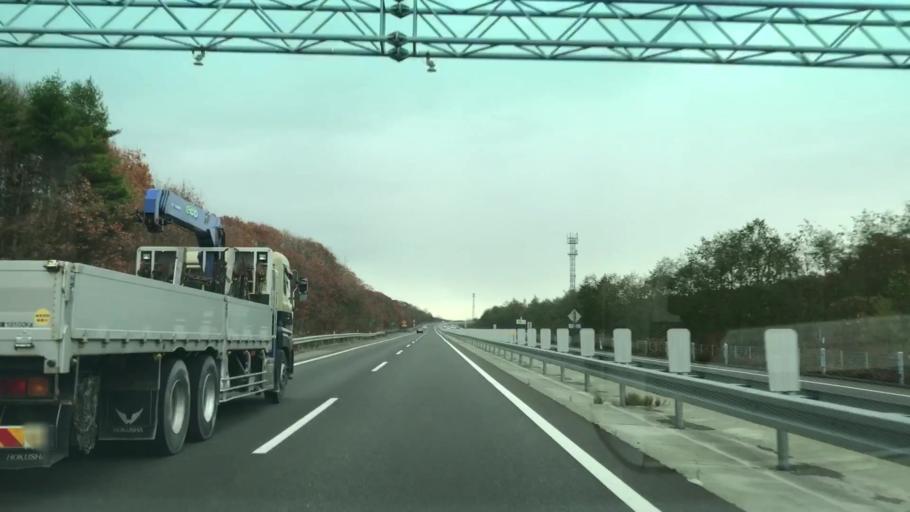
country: JP
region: Hokkaido
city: Tomakomai
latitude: 42.6594
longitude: 141.8200
